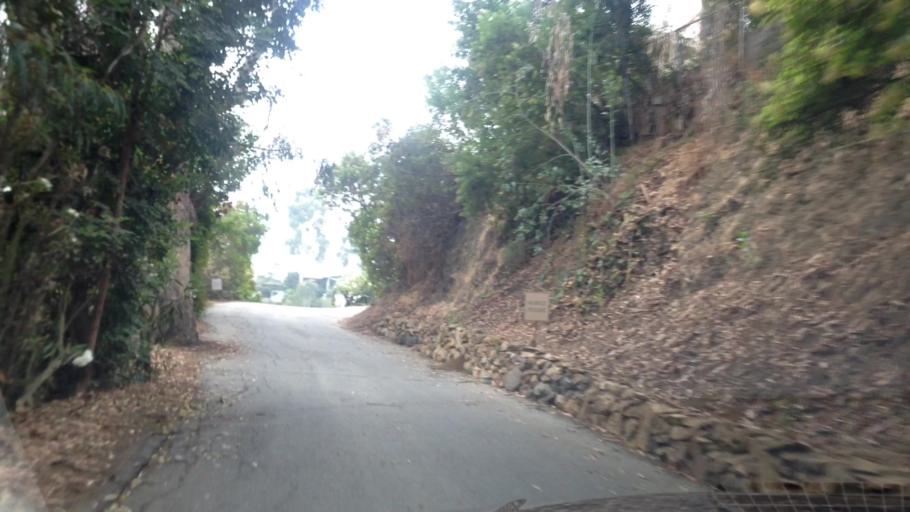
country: US
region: California
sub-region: Los Angeles County
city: Universal City
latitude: 34.1170
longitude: -118.3471
